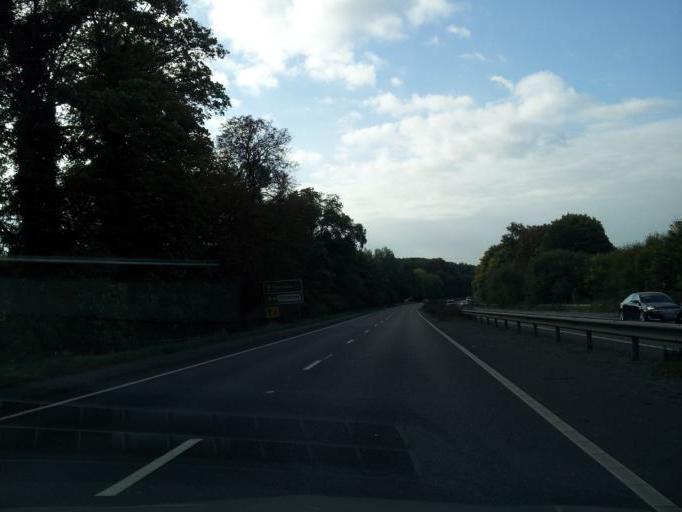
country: GB
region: England
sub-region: Northamptonshire
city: Towcester
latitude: 52.1547
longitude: -0.9664
